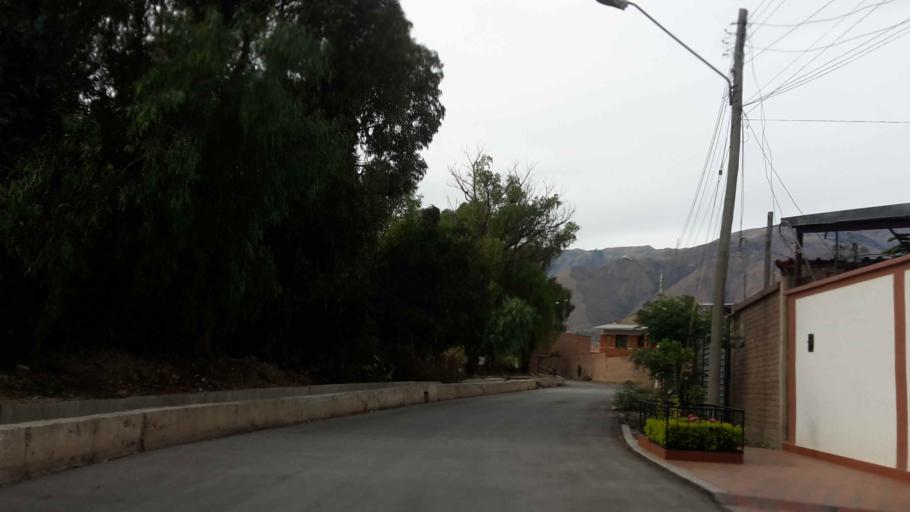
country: BO
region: Cochabamba
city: Cochabamba
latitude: -17.3603
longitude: -66.1911
